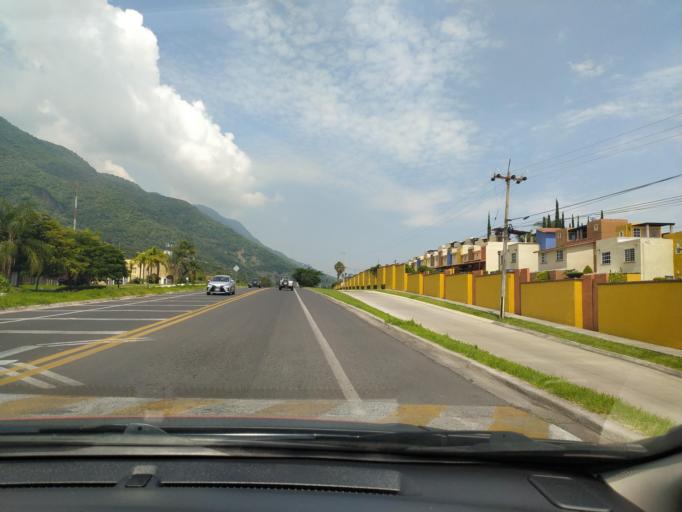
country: MX
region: Jalisco
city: Jocotepec
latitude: 20.2939
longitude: -103.3878
